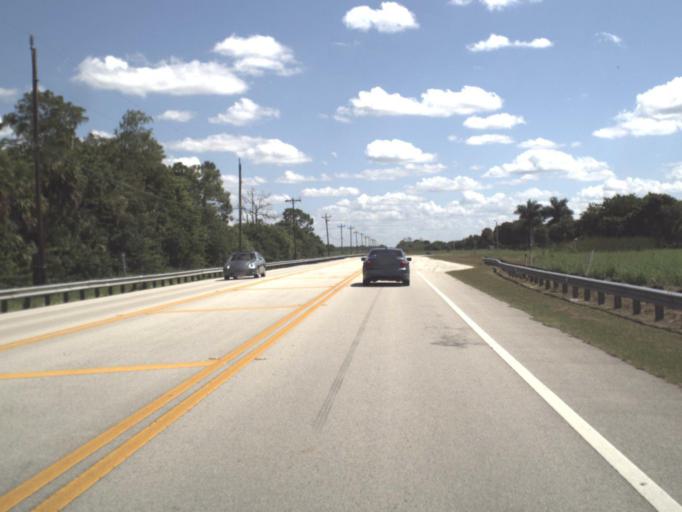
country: US
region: Florida
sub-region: Collier County
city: Lely Resort
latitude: 26.0182
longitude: -81.6287
